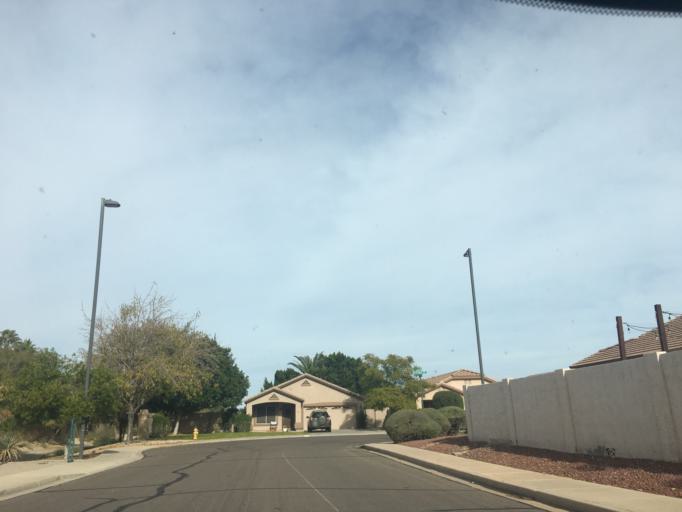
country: US
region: Arizona
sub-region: Maricopa County
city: Gilbert
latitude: 33.3540
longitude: -111.8094
